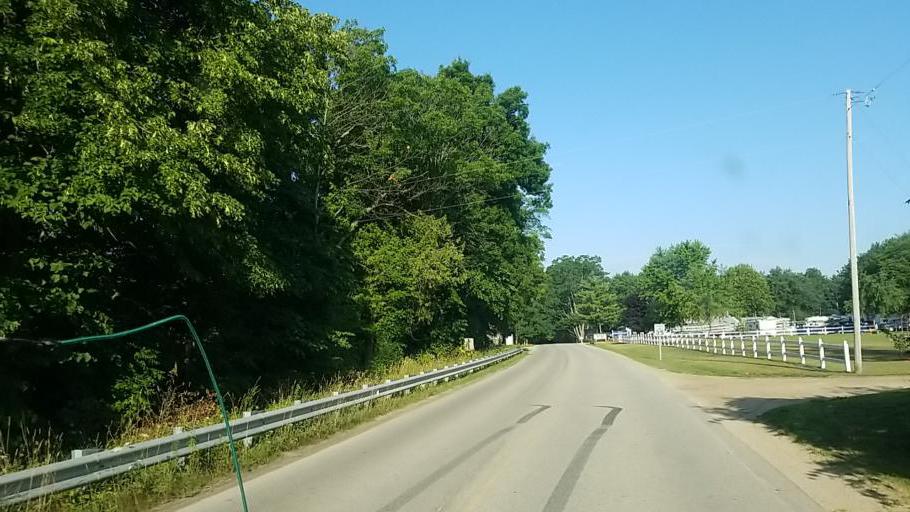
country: US
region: Michigan
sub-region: Newaygo County
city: Fremont
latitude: 43.3467
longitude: -85.9344
